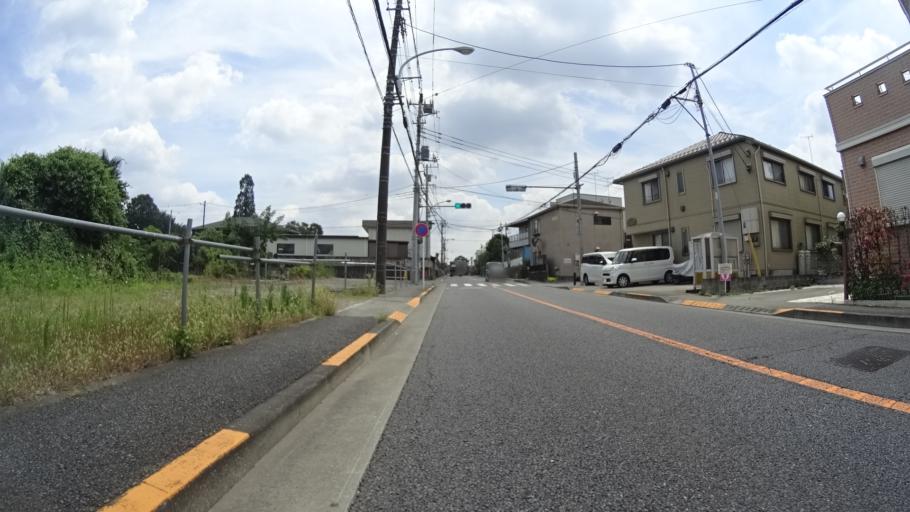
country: JP
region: Tokyo
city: Fussa
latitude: 35.7695
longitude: 139.2986
